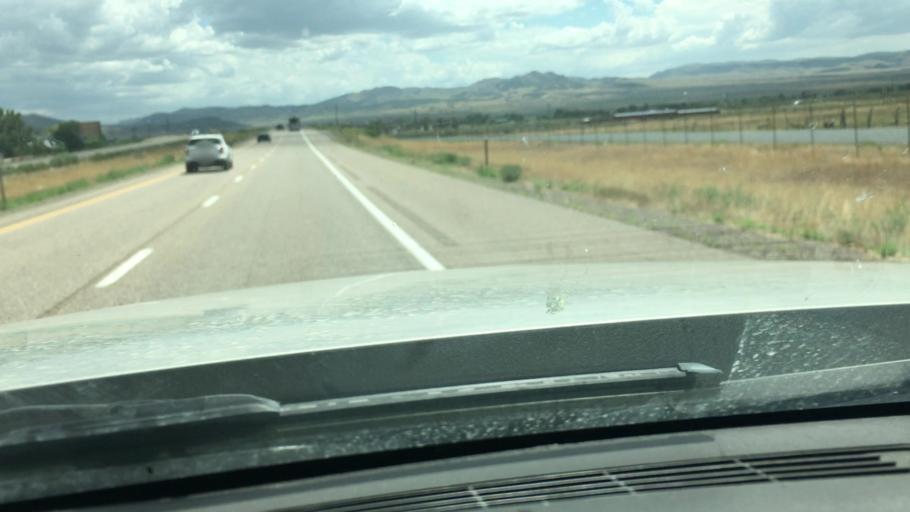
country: US
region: Utah
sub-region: Beaver County
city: Beaver
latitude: 38.2775
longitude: -112.6508
